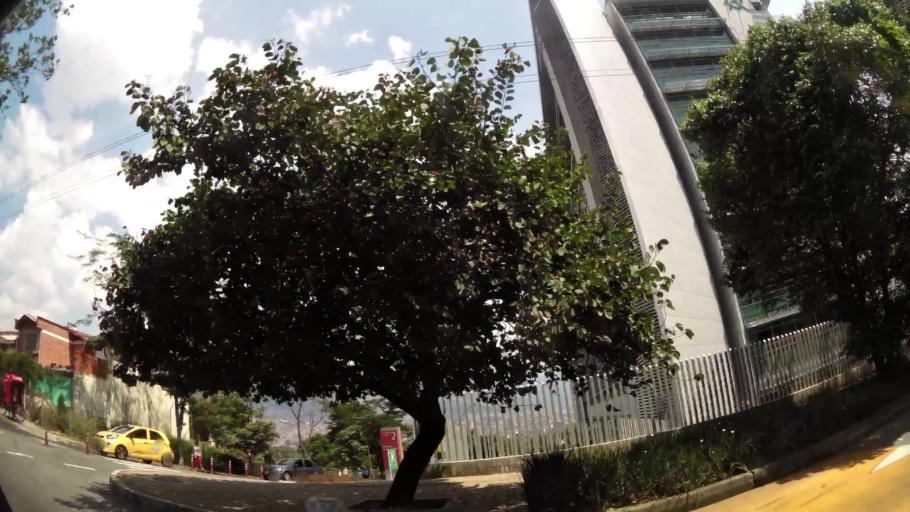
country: CO
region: Antioquia
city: Medellin
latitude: 6.2785
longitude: -75.5802
